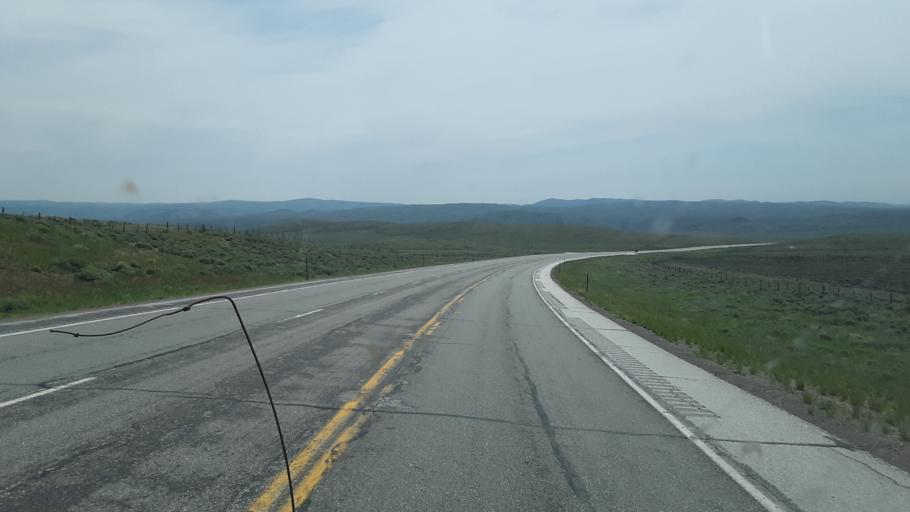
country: US
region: Wyoming
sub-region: Carbon County
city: Saratoga
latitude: 41.1289
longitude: -106.5531
